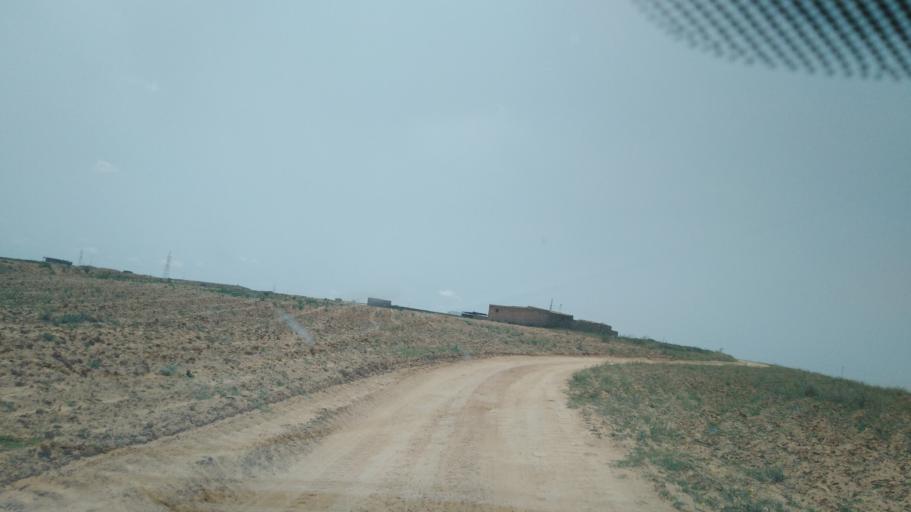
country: TN
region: Safaqis
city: Sfax
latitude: 34.7707
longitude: 10.5785
